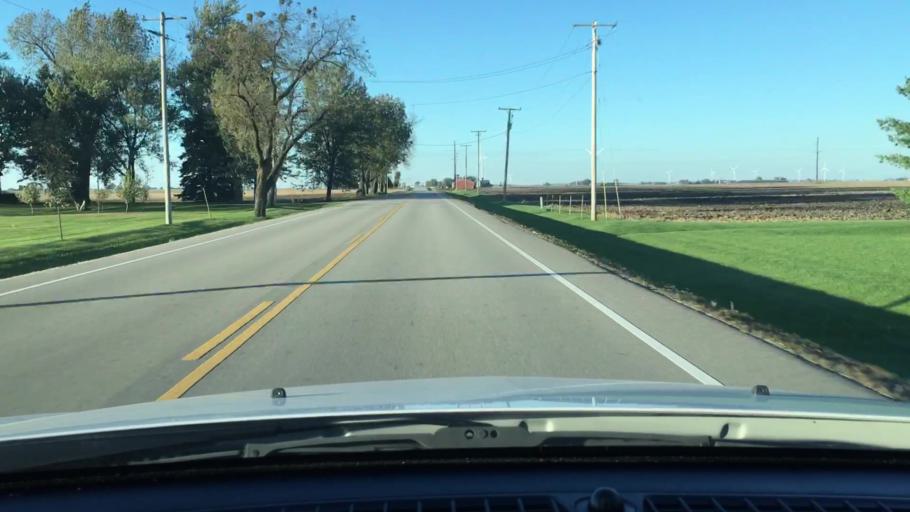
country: US
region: Illinois
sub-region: DeKalb County
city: Malta
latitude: 41.8229
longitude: -88.8864
